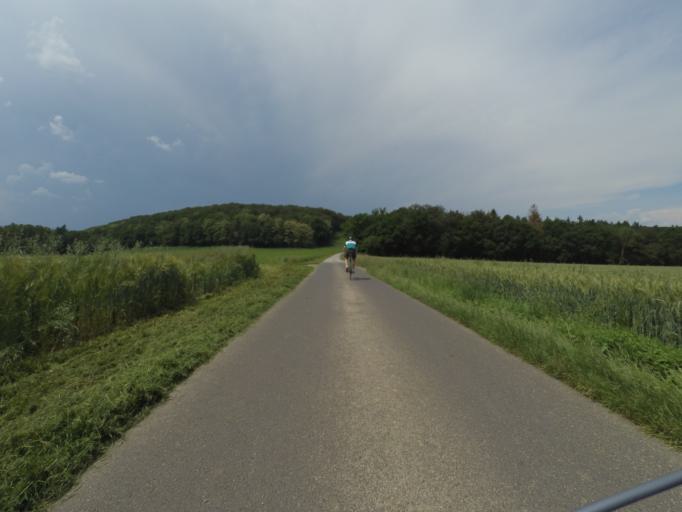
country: DE
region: Rheinland-Pfalz
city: Morshausen
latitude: 50.2060
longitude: 7.4334
